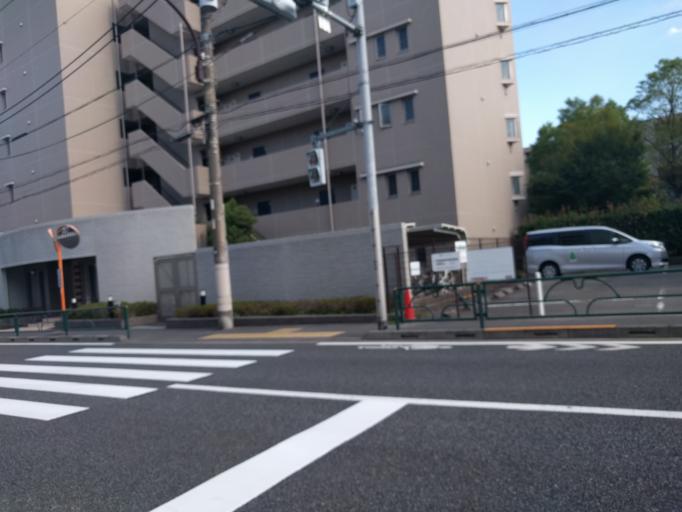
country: JP
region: Tokyo
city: Tokyo
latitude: 35.6301
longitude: 139.6394
